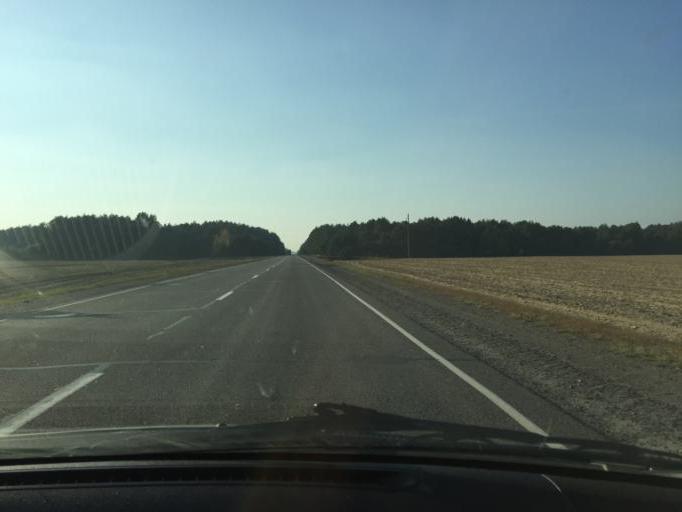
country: BY
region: Brest
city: Davyd-Haradok
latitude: 52.2464
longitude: 27.1112
